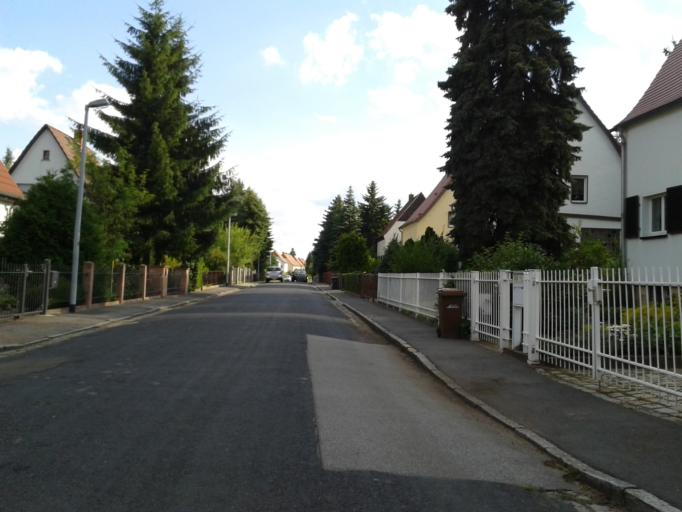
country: DE
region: Saxony
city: Albertstadt
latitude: 51.1147
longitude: 13.7416
